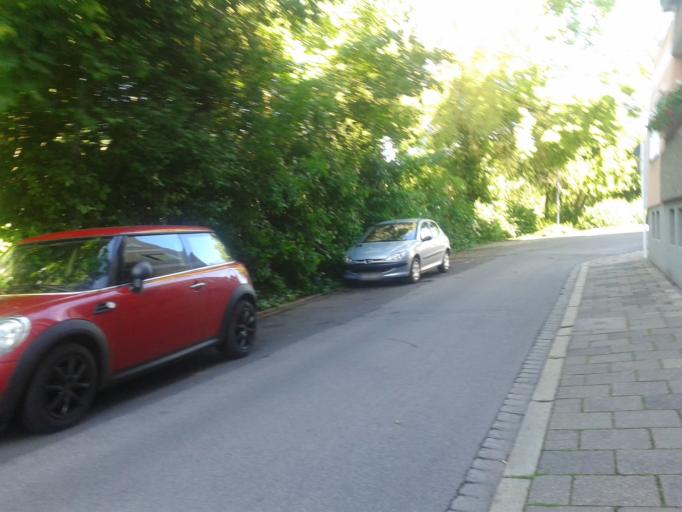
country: DE
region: Bavaria
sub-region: Upper Franconia
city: Bamberg
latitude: 49.8953
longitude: 10.8810
